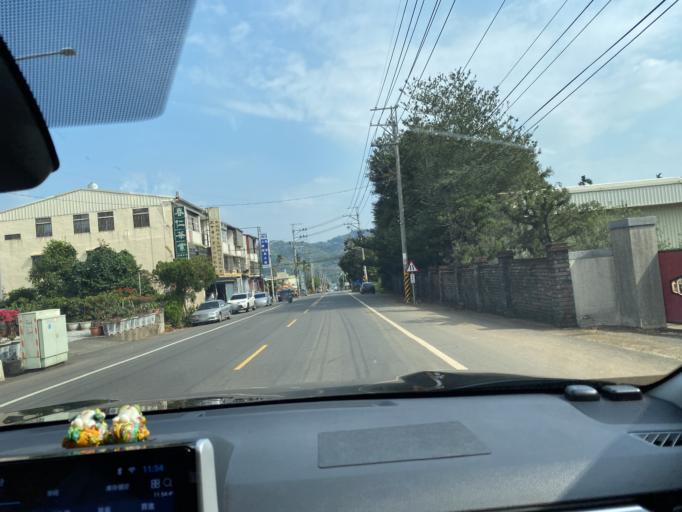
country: TW
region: Taiwan
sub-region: Nantou
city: Nantou
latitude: 23.8412
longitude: 120.6887
